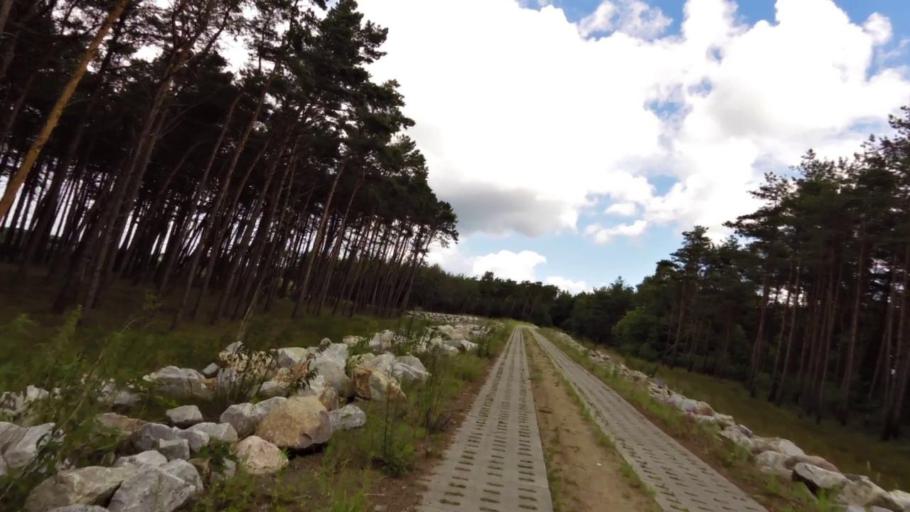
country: PL
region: West Pomeranian Voivodeship
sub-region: Powiat slawienski
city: Darlowo
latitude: 54.4897
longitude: 16.4381
